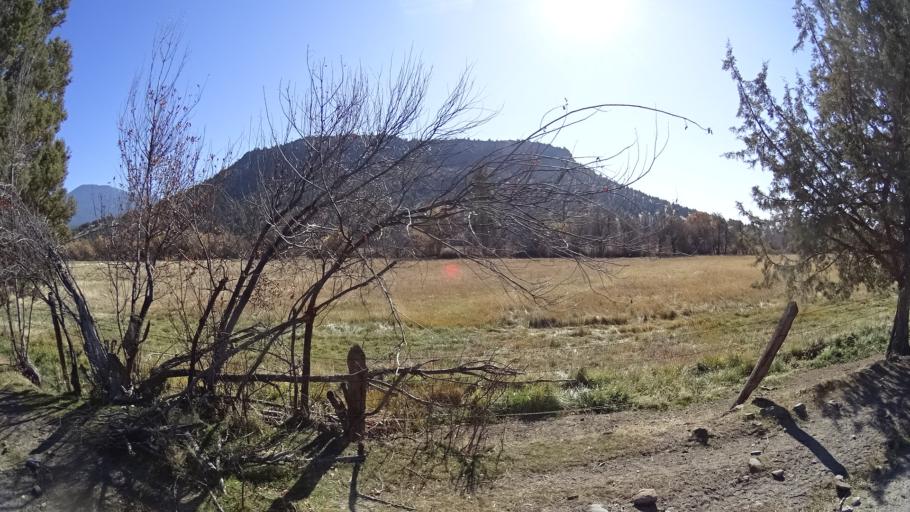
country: US
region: California
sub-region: Siskiyou County
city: Montague
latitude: 41.7384
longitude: -122.3431
